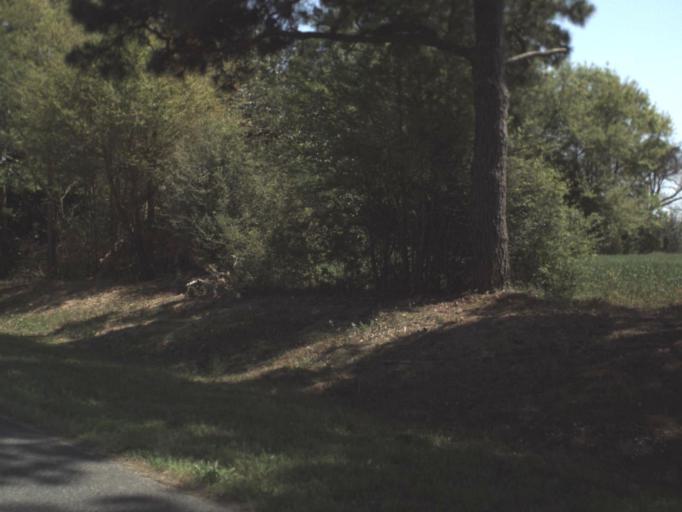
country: US
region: Florida
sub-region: Escambia County
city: Century
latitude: 30.9523
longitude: -87.1251
